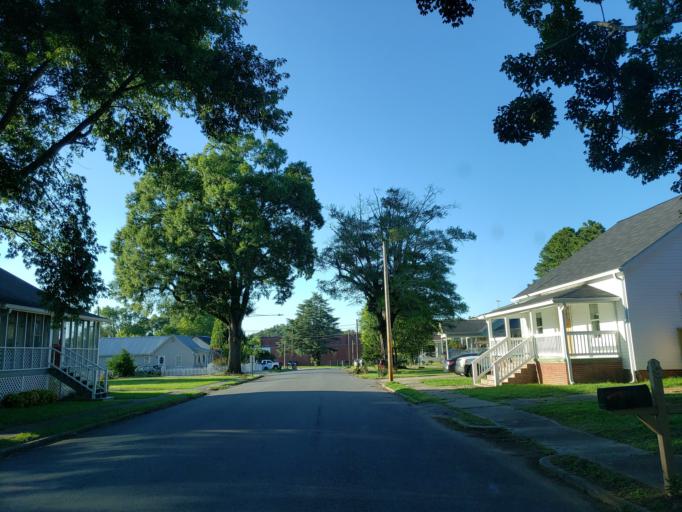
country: US
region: Georgia
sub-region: Polk County
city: Aragon
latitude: 34.0461
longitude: -85.0561
